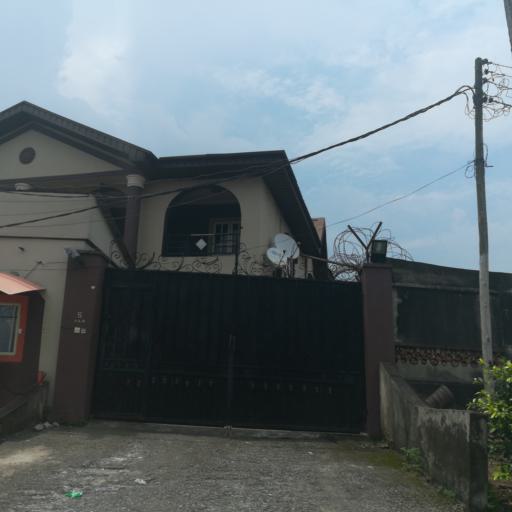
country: NG
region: Lagos
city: Ojota
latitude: 6.5735
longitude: 3.3852
